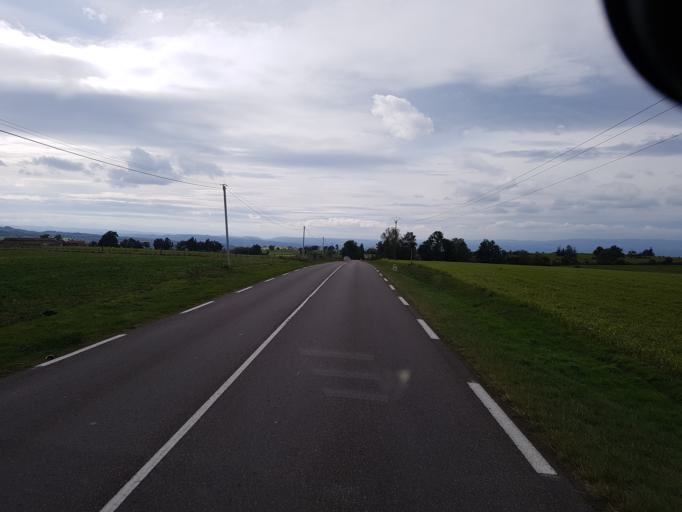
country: FR
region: Rhone-Alpes
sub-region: Departement de la Loire
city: Chazelles-sur-Lyon
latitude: 45.6268
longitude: 4.3508
